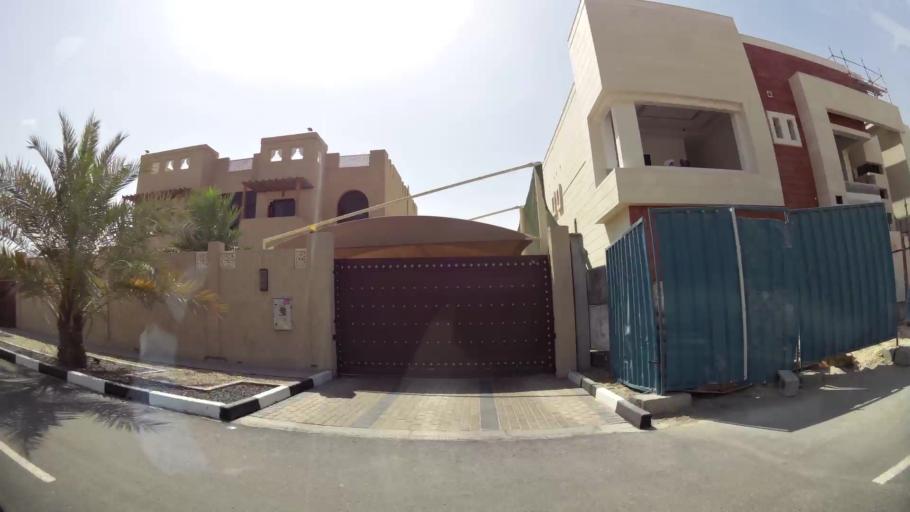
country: AE
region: Ash Shariqah
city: Sharjah
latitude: 25.2038
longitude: 55.4224
